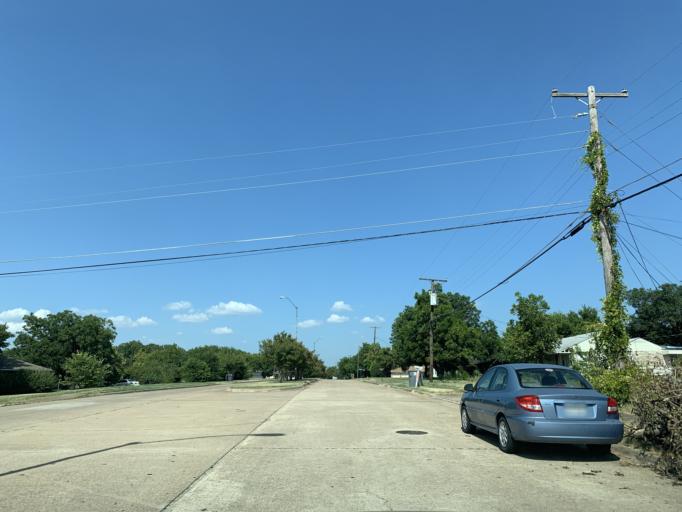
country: US
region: Texas
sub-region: Dallas County
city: Hutchins
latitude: 32.6549
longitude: -96.7799
